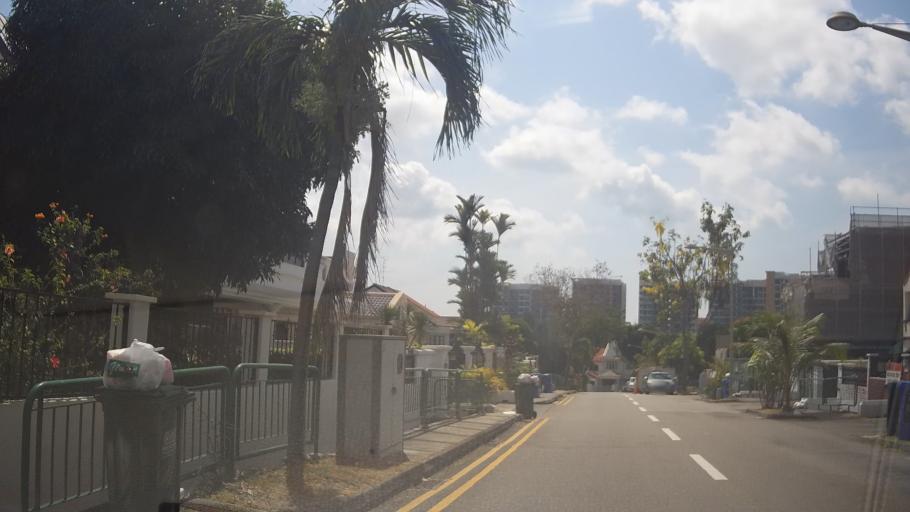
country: SG
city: Singapore
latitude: 1.3306
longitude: 103.9471
